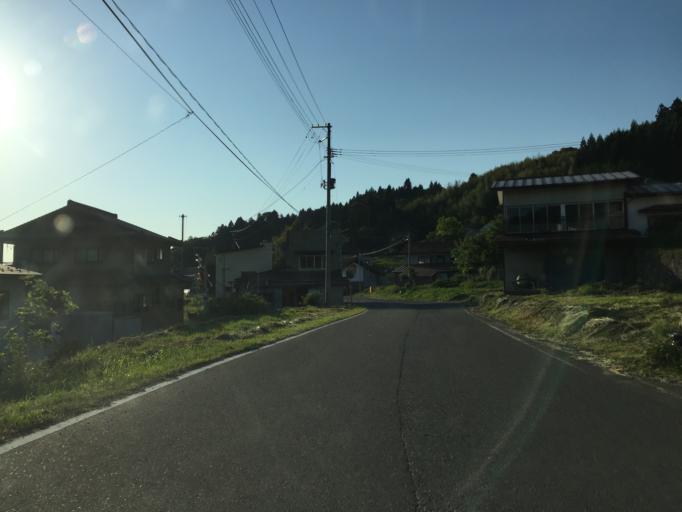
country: JP
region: Fukushima
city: Ishikawa
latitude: 37.0435
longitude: 140.4346
